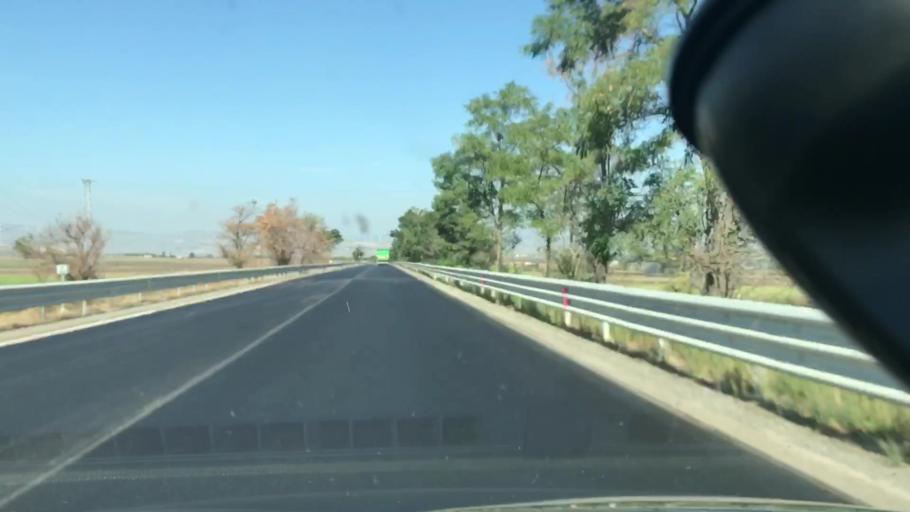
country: IT
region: Basilicate
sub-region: Provincia di Potenza
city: Zona 179
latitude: 41.0773
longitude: 15.6376
